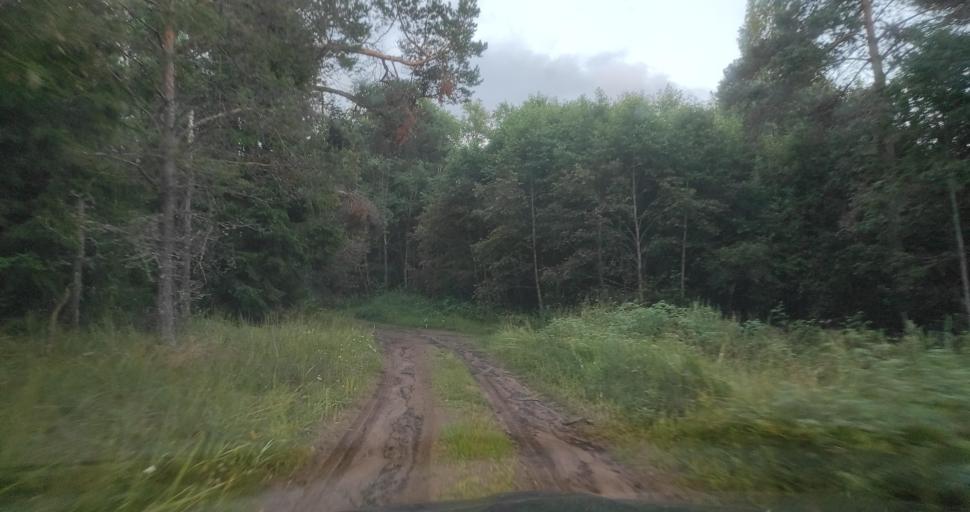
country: LV
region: Kuldigas Rajons
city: Kuldiga
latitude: 57.0638
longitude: 21.8640
